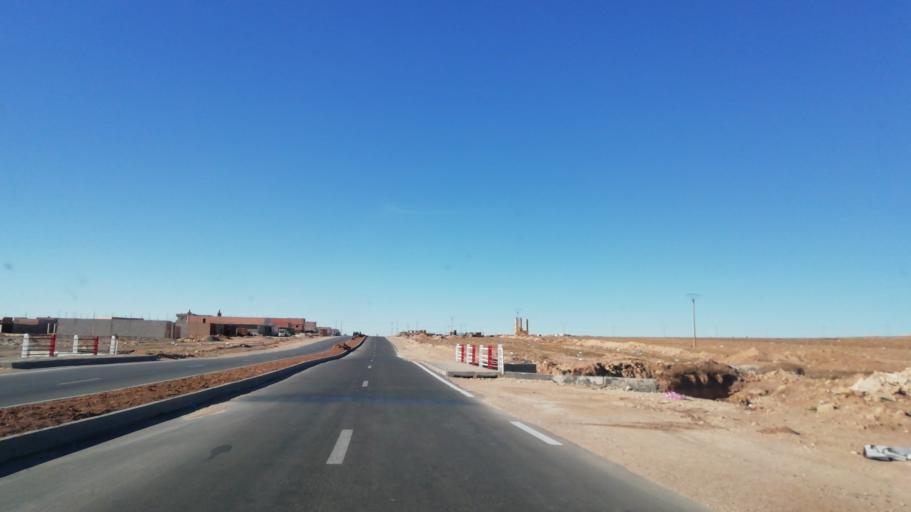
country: DZ
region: Tlemcen
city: Sebdou
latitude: 34.2152
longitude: -1.2446
